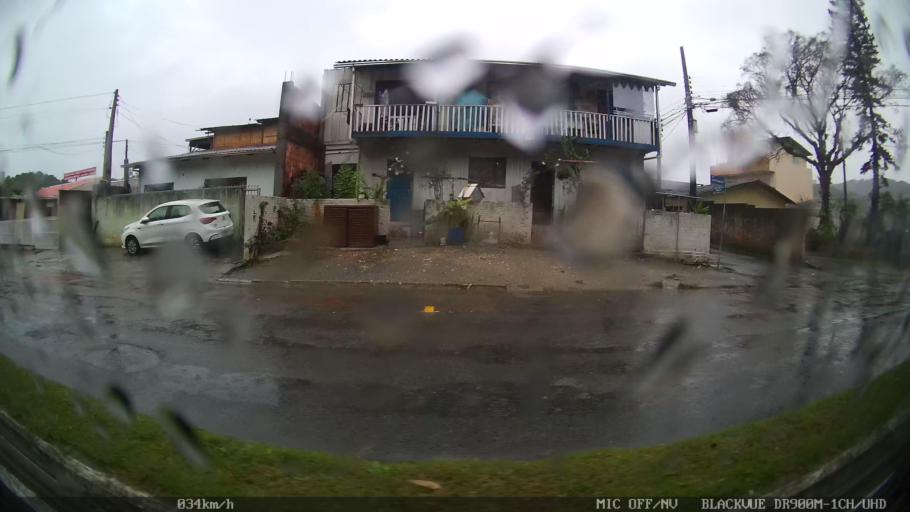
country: BR
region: Santa Catarina
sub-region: Itajai
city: Itajai
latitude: -26.9443
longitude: -48.6369
